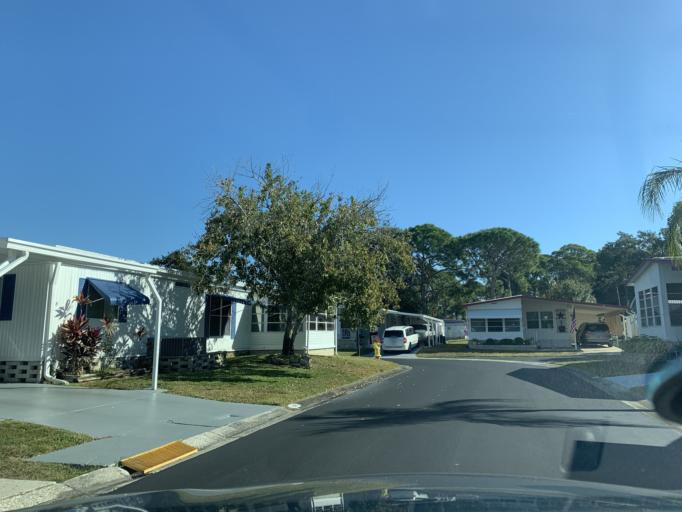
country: US
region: Florida
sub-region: Pinellas County
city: Kenneth City
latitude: 27.8157
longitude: -82.7463
